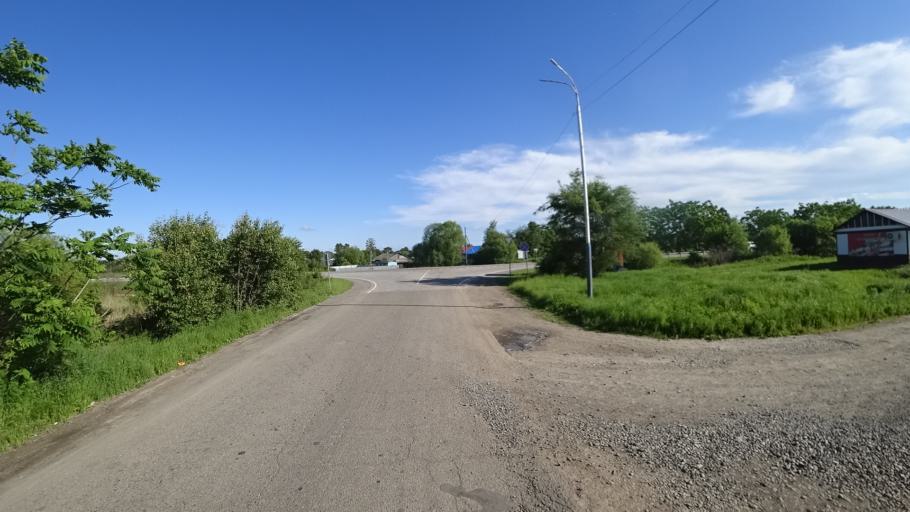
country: RU
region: Khabarovsk Krai
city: Khor
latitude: 47.8912
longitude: 134.9915
